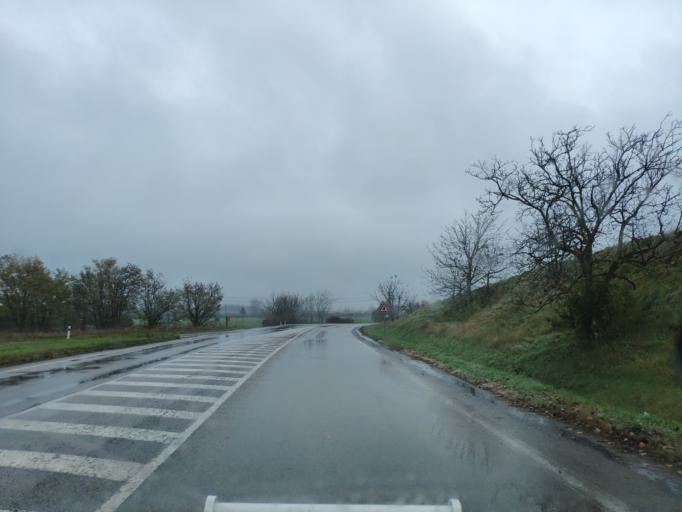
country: HU
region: Borsod-Abauj-Zemplen
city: Ricse
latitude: 48.4299
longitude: 21.9837
